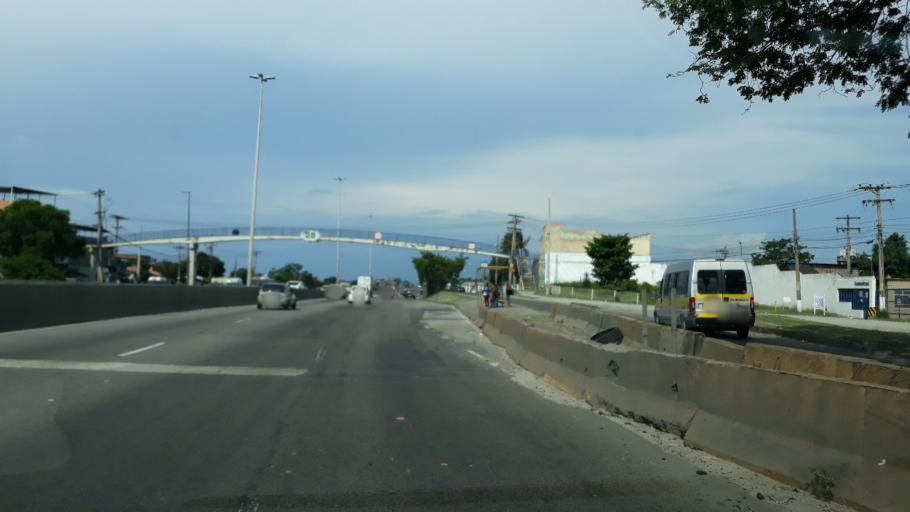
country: BR
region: Rio de Janeiro
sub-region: Sao Joao De Meriti
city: Sao Joao de Meriti
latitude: -22.8315
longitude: -43.3516
